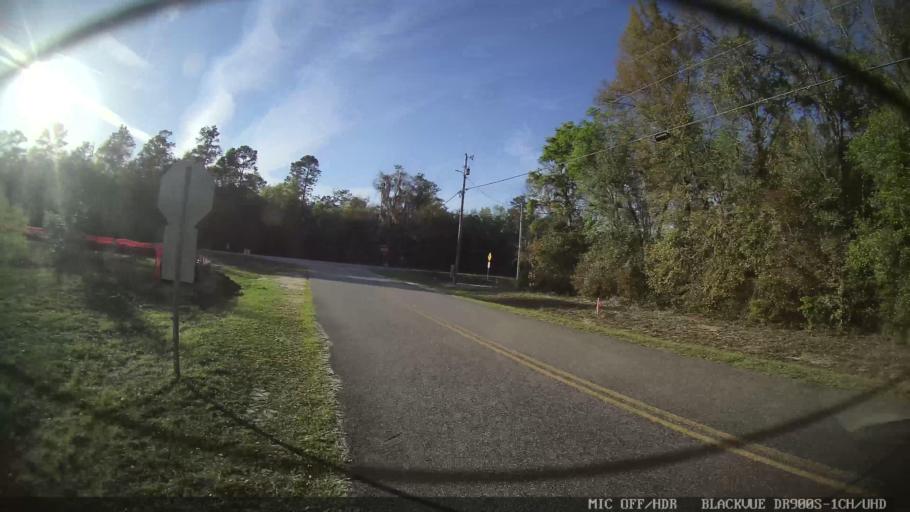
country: US
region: Georgia
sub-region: Echols County
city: Statenville
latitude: 30.6487
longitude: -83.1834
